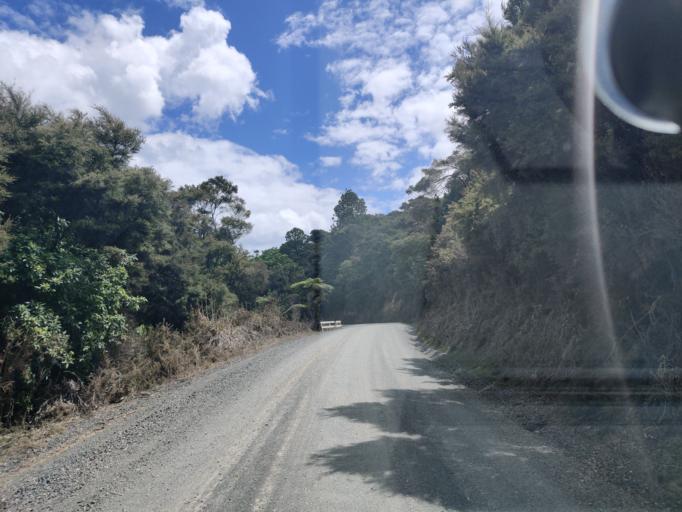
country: NZ
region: Northland
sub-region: Far North District
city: Paihia
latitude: -35.2605
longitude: 174.0503
